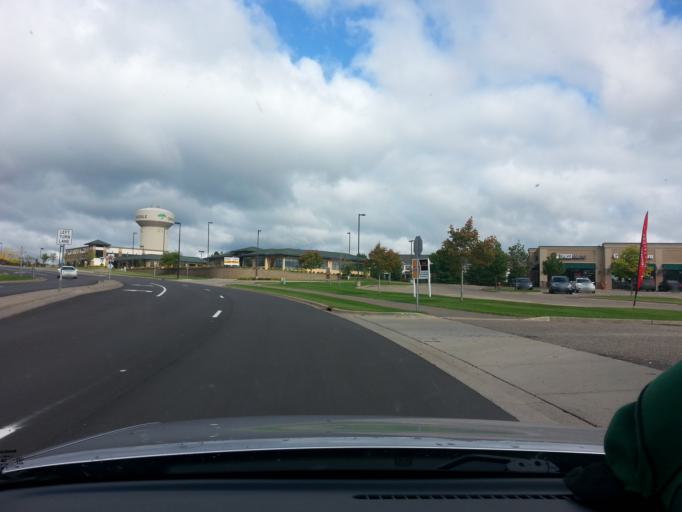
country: US
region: Minnesota
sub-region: Washington County
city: Oakdale
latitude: 44.9641
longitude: -92.9516
